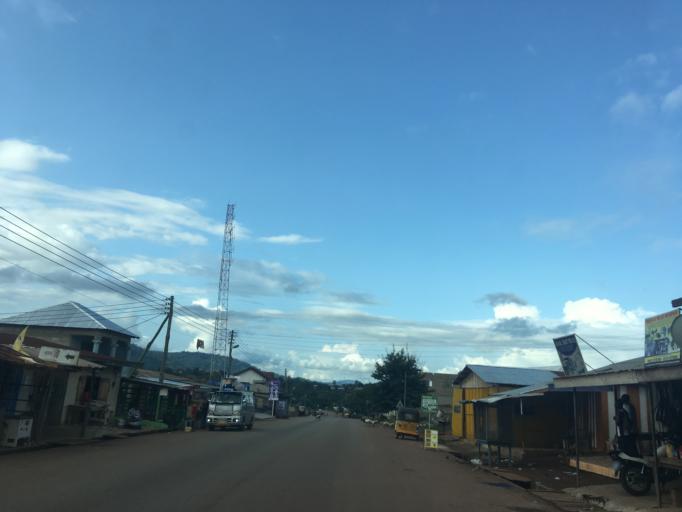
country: GH
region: Western
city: Bibiani
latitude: 6.1968
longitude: -2.3207
